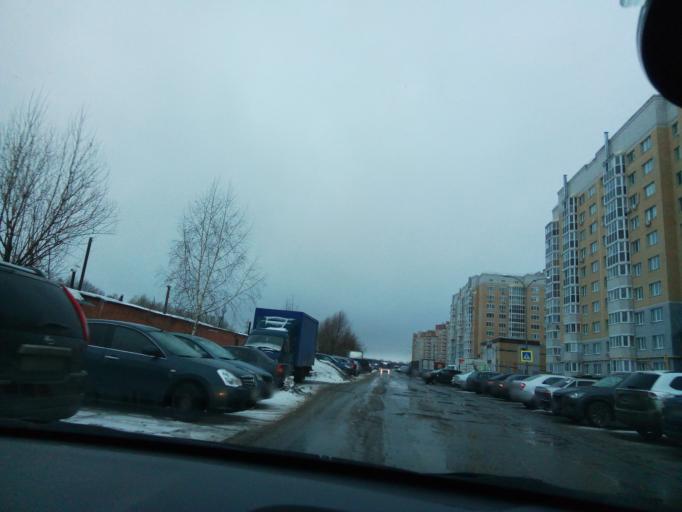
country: RU
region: Chuvashia
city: Novyye Lapsary
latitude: 56.1312
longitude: 47.1580
